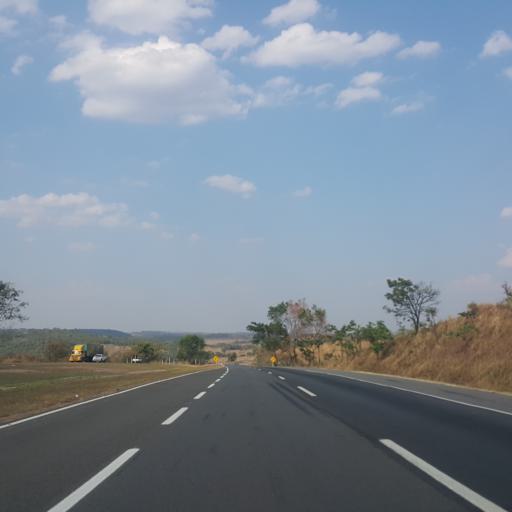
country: BR
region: Goias
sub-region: Abadiania
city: Abadiania
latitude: -16.1105
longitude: -48.5711
